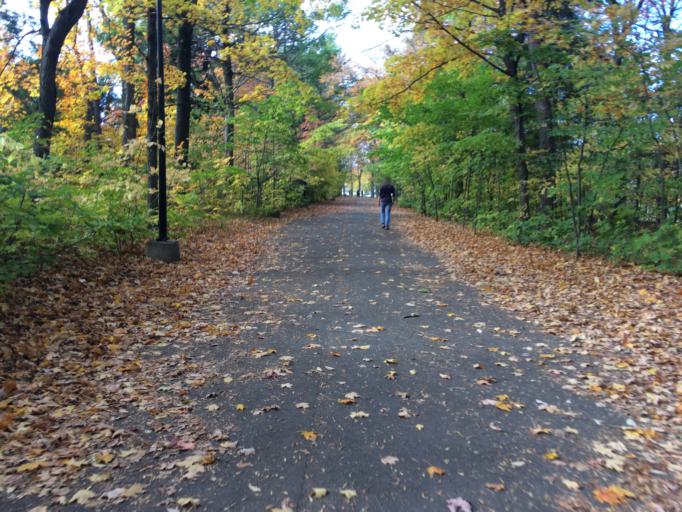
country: CA
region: Quebec
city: Quebec
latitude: 46.7886
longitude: -71.2433
